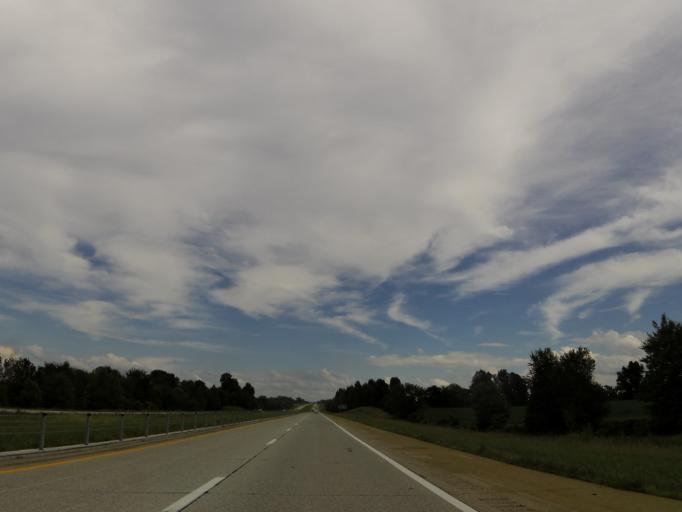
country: US
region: Kentucky
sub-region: Caldwell County
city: Princeton
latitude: 36.9828
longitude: -87.9176
